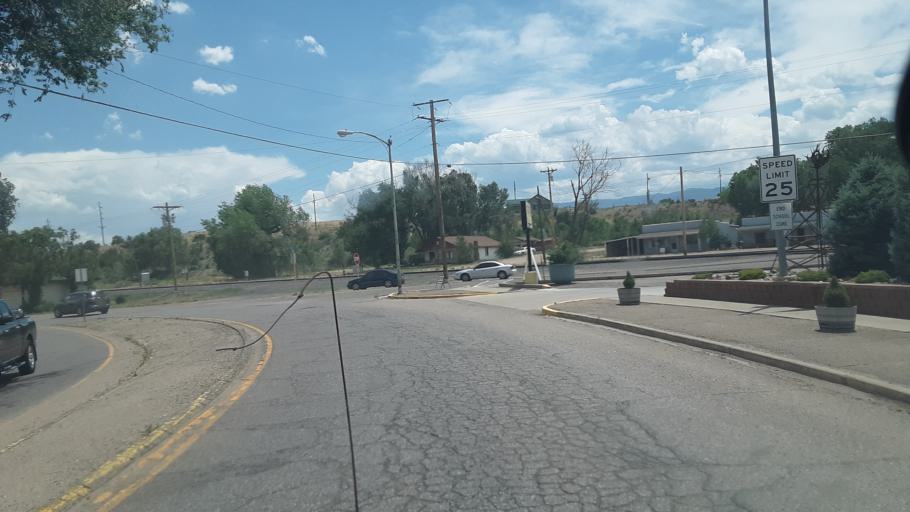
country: US
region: Colorado
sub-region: Fremont County
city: Florence
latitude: 38.3913
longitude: -105.1226
